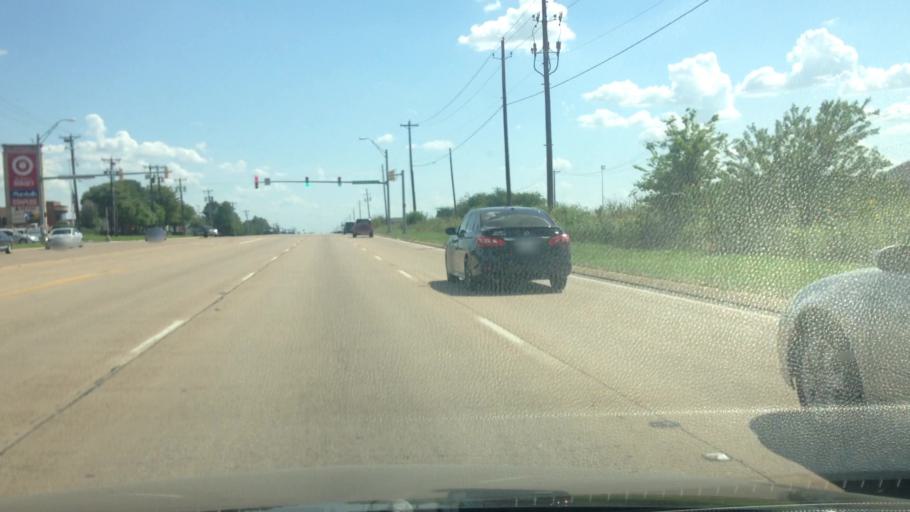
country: US
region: Texas
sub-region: Tarrant County
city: Watauga
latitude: 32.8931
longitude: -97.2590
